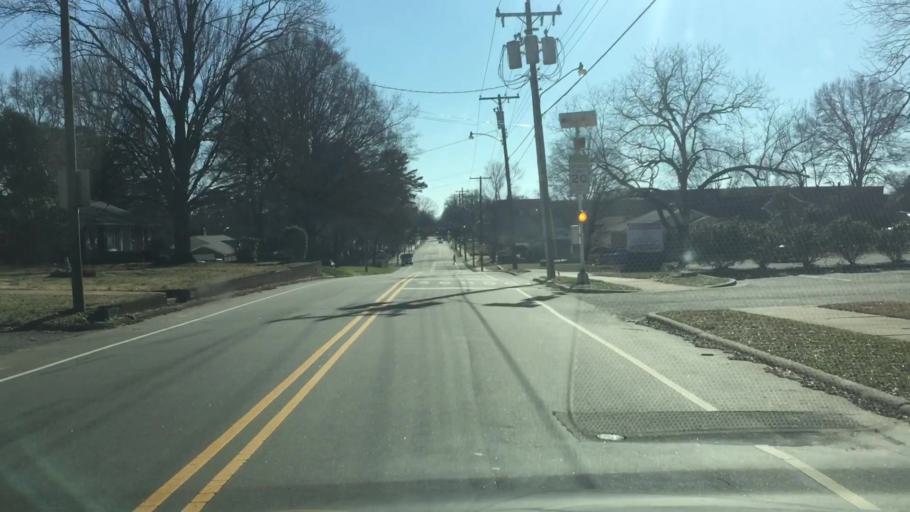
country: US
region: North Carolina
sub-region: Iredell County
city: Mooresville
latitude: 35.5803
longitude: -80.8009
